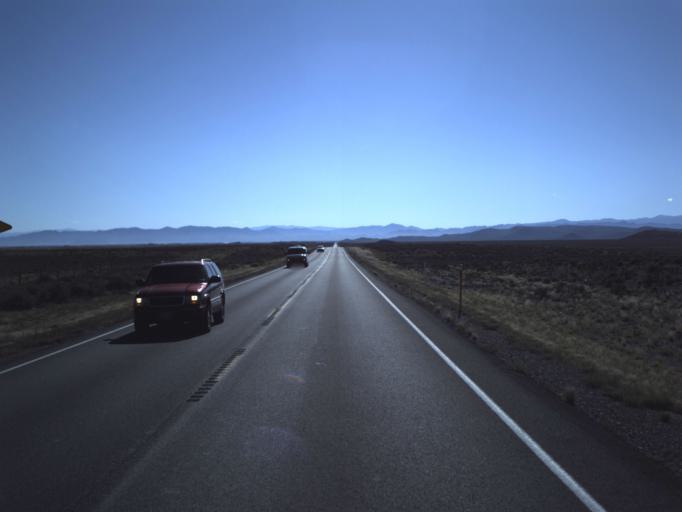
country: US
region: Utah
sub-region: Washington County
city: Enterprise
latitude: 37.7874
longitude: -113.8787
